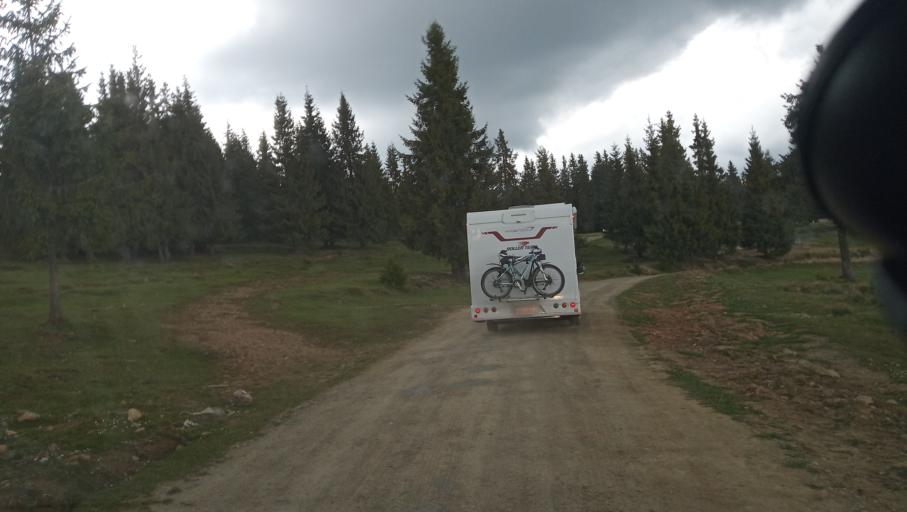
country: RO
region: Cluj
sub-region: Comuna Belis
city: Belis
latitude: 46.6346
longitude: 23.0433
